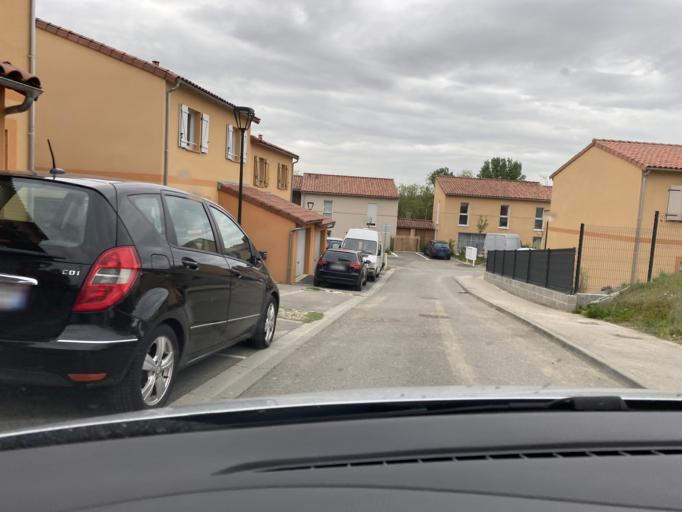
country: FR
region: Midi-Pyrenees
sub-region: Departement de la Haute-Garonne
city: Montgiscard
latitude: 43.4743
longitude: 1.5482
